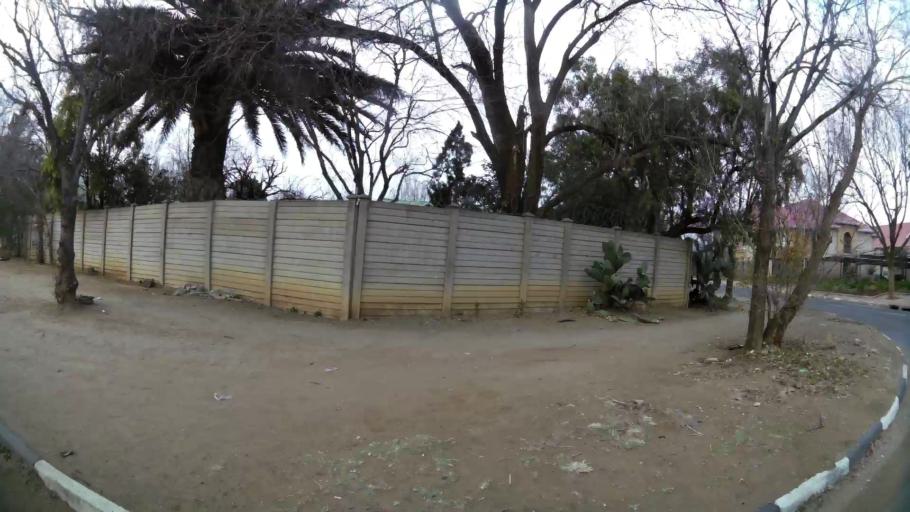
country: ZA
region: Orange Free State
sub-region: Mangaung Metropolitan Municipality
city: Bloemfontein
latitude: -29.1178
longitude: 26.1896
